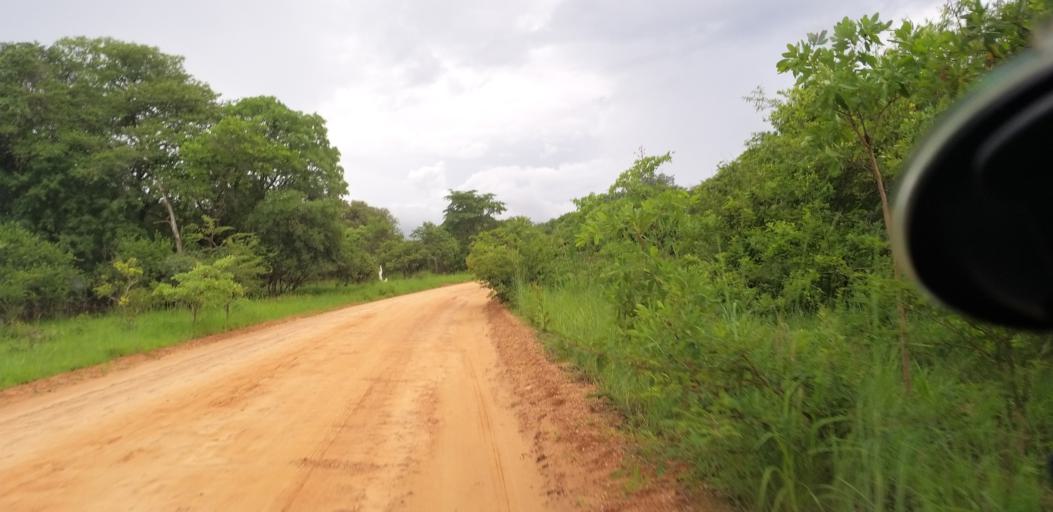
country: ZM
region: Lusaka
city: Chongwe
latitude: -15.1570
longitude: 28.4983
